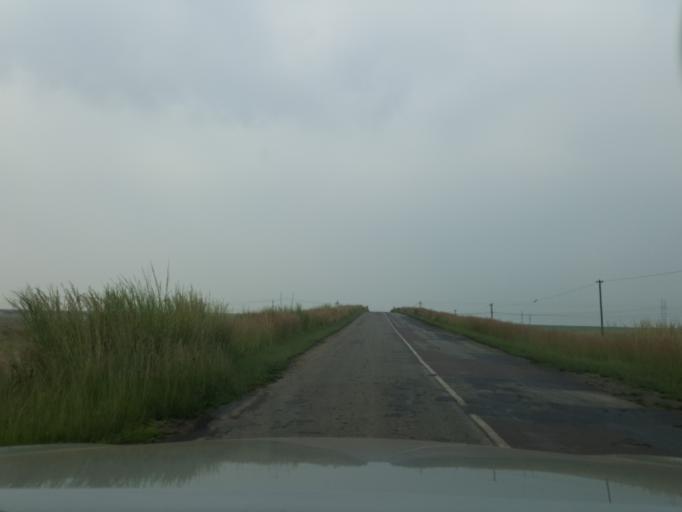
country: ZA
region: Mpumalanga
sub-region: Nkangala District Municipality
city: Middelburg
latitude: -26.0107
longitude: 29.4497
